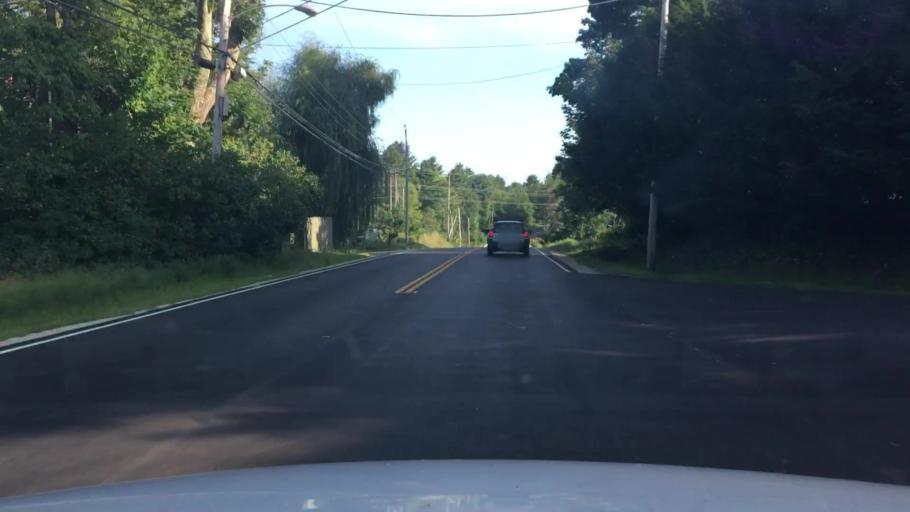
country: US
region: Maine
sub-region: Cumberland County
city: Cumberland Center
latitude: 43.8019
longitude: -70.3082
